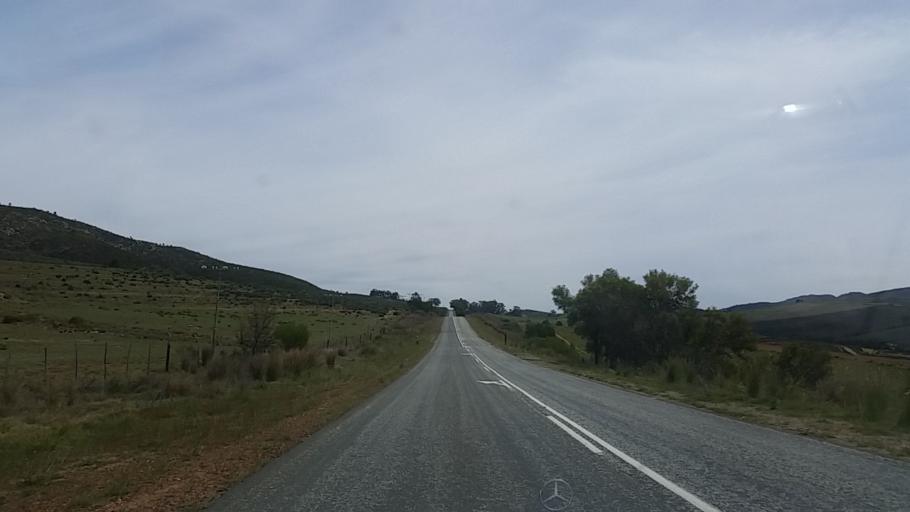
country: ZA
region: Western Cape
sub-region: Eden District Municipality
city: Knysna
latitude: -33.7725
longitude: 22.9376
